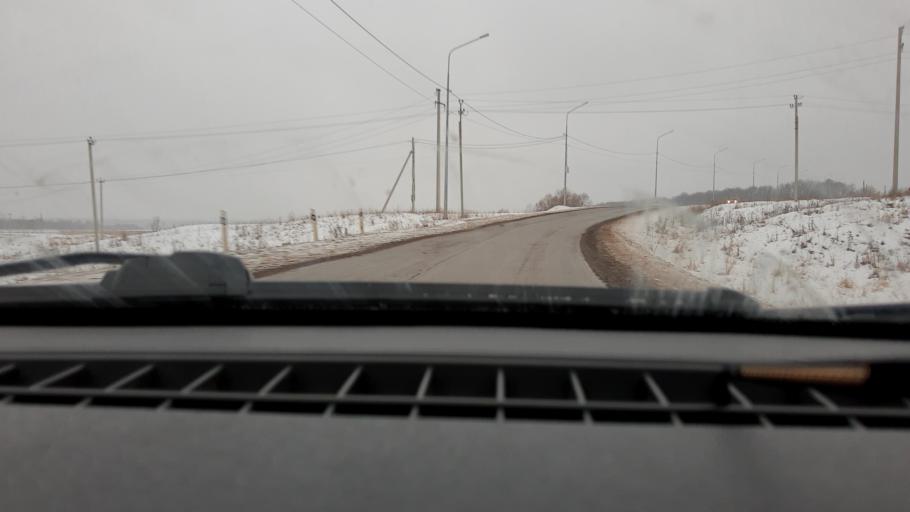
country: RU
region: Bashkortostan
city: Kabakovo
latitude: 54.7042
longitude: 56.2370
